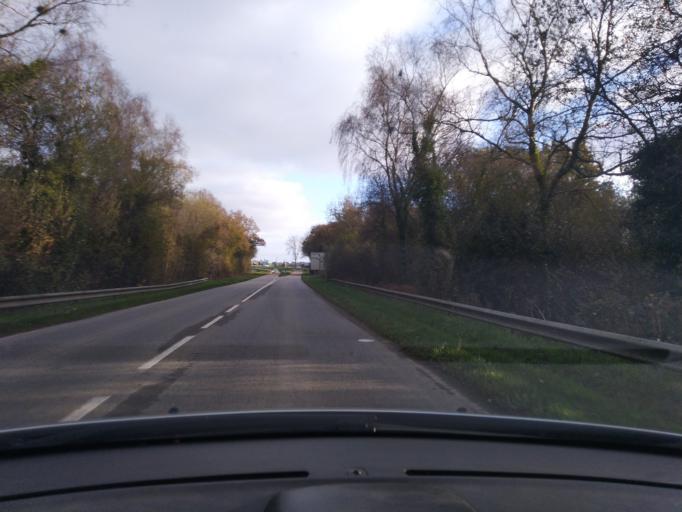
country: FR
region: Brittany
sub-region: Departement du Finistere
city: Morlaix
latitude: 48.5814
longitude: -3.8004
